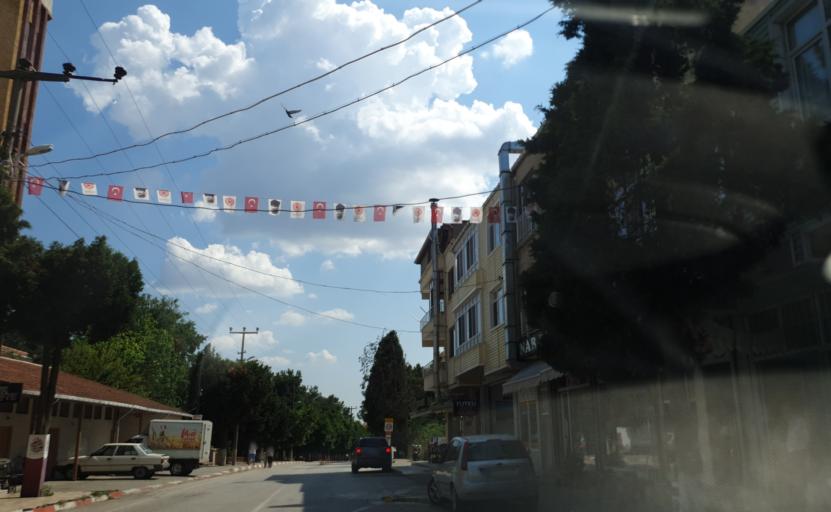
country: TR
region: Kirklareli
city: Buyukkaristiran
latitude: 41.4381
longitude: 27.5850
